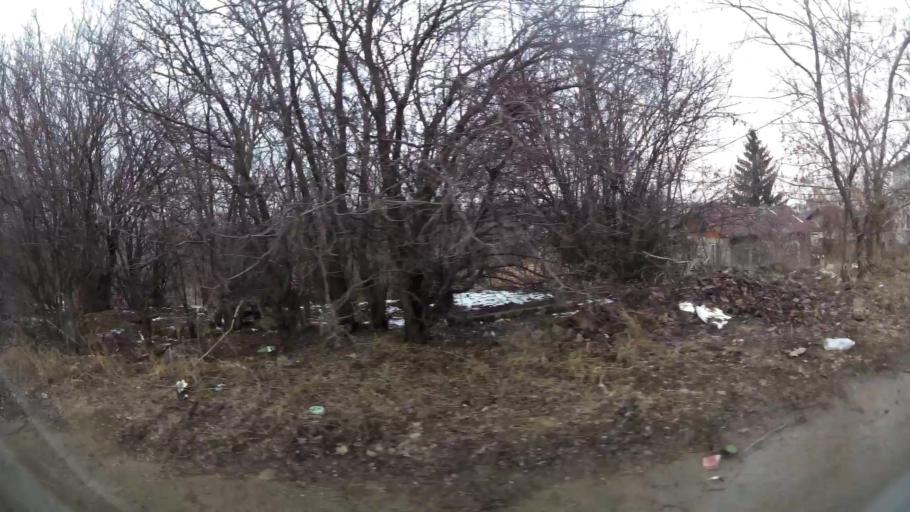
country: BG
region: Sofiya
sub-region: Obshtina Bozhurishte
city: Bozhurishte
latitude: 42.6946
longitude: 23.2190
